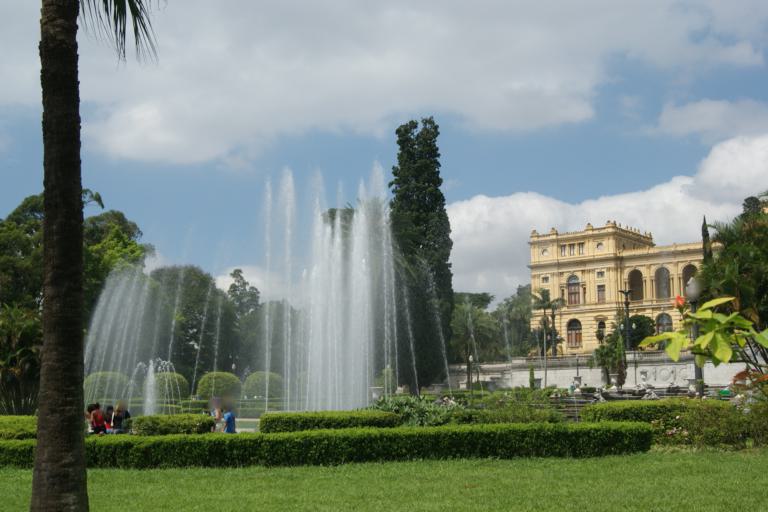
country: BR
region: Sao Paulo
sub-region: Sao Paulo
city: Sao Paulo
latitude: -23.5842
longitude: -46.6102
